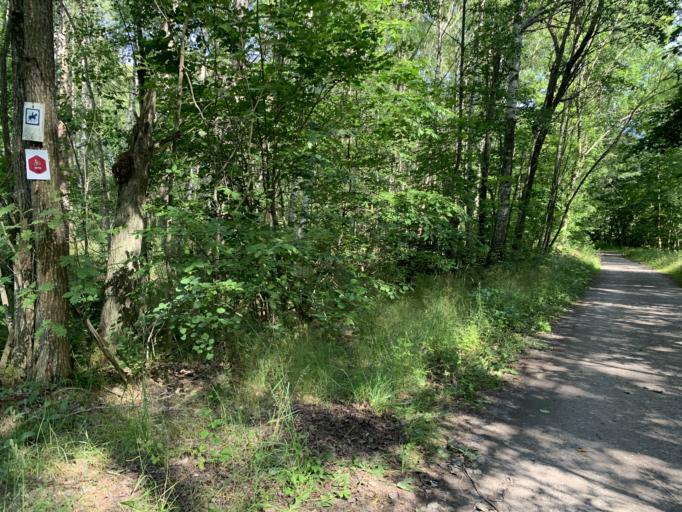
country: SE
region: Stockholm
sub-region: Stockholms Kommun
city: Kista
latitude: 59.3981
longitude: 17.9742
